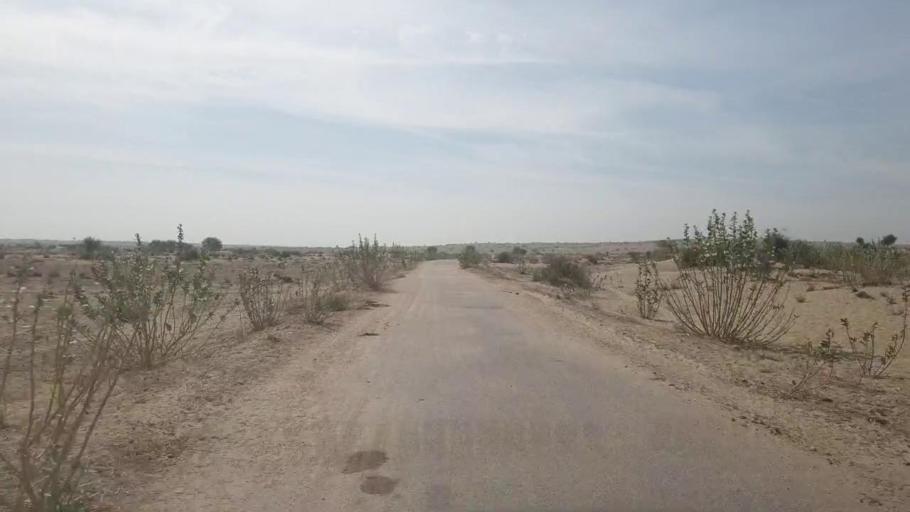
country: PK
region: Sindh
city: Umarkot
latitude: 25.2867
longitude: 69.7286
